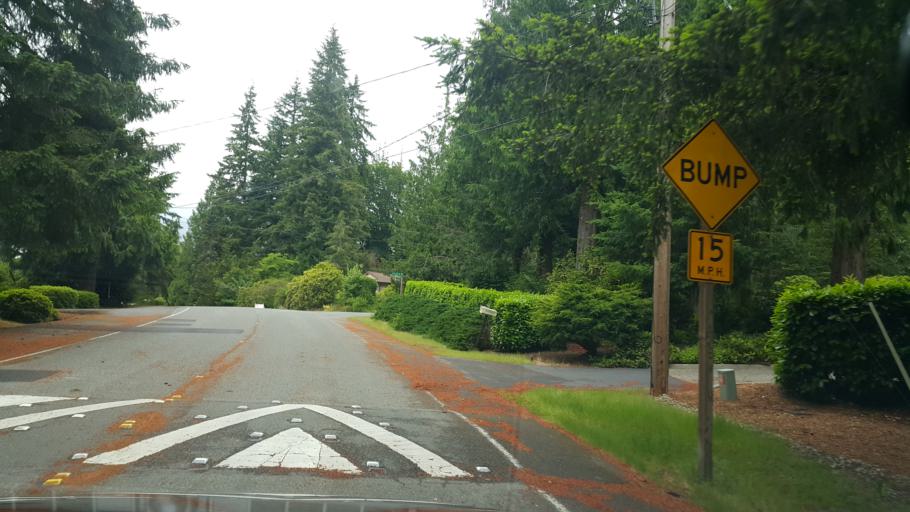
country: US
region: Washington
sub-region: King County
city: Fairwood
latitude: 47.4378
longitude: -122.1444
